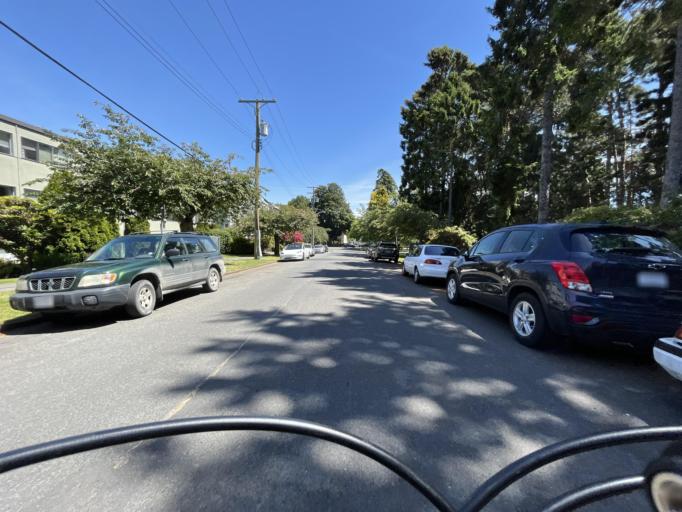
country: CA
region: British Columbia
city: Victoria
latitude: 48.4128
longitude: -123.3587
